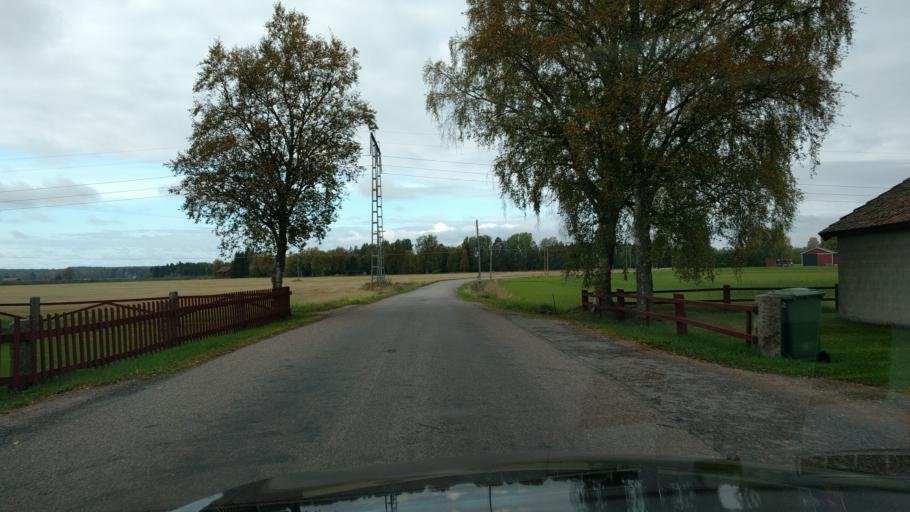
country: SE
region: Uppsala
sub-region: Osthammars Kommun
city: Bjorklinge
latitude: 60.1572
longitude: 17.5487
